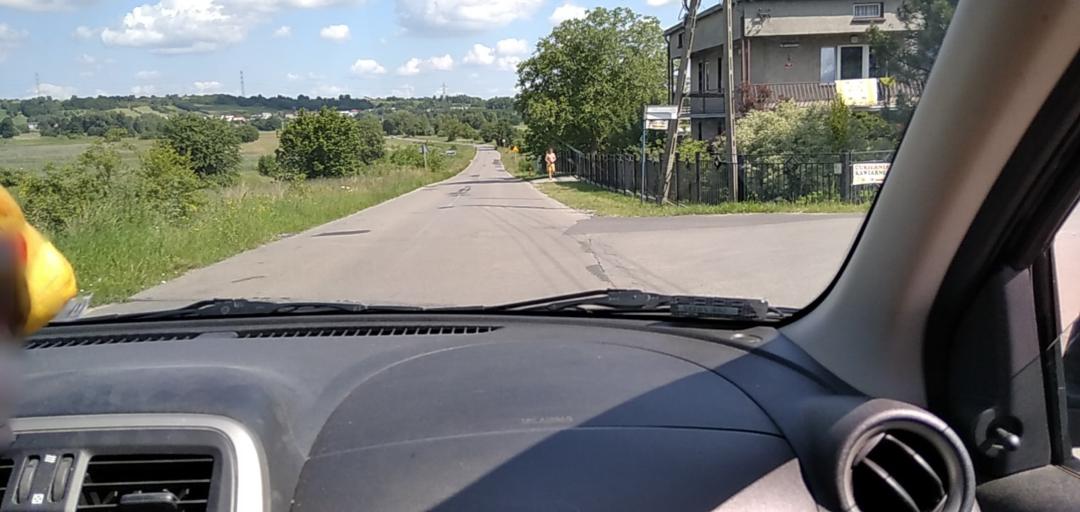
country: PL
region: Silesian Voivodeship
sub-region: Powiat bedzinski
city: Sarnow
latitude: 50.3924
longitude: 19.1394
